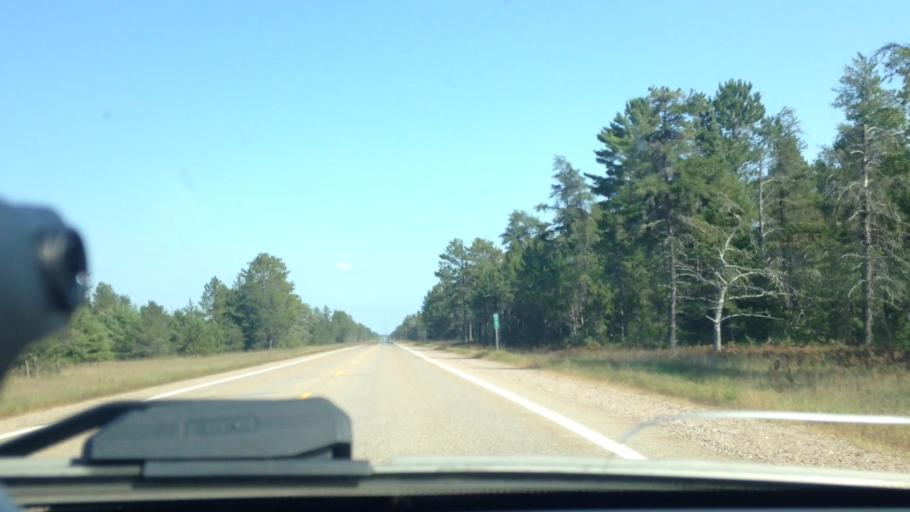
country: US
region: Michigan
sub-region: Mackinac County
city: Saint Ignace
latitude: 46.3586
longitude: -84.8441
